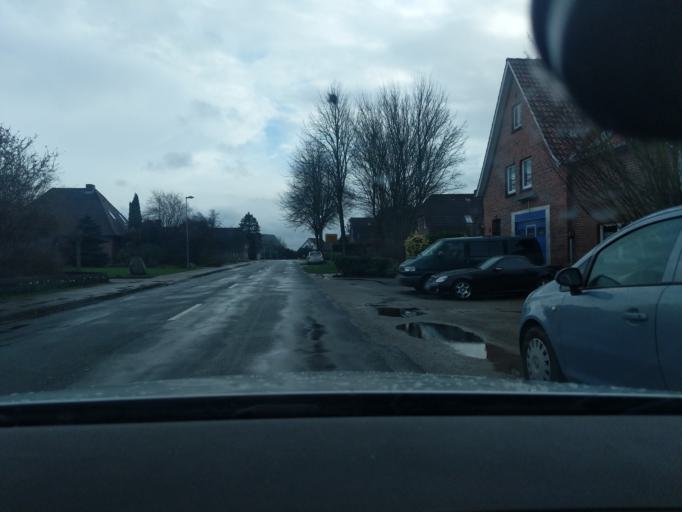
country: DE
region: Lower Saxony
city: Agathenburg
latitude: 53.5936
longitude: 9.5511
